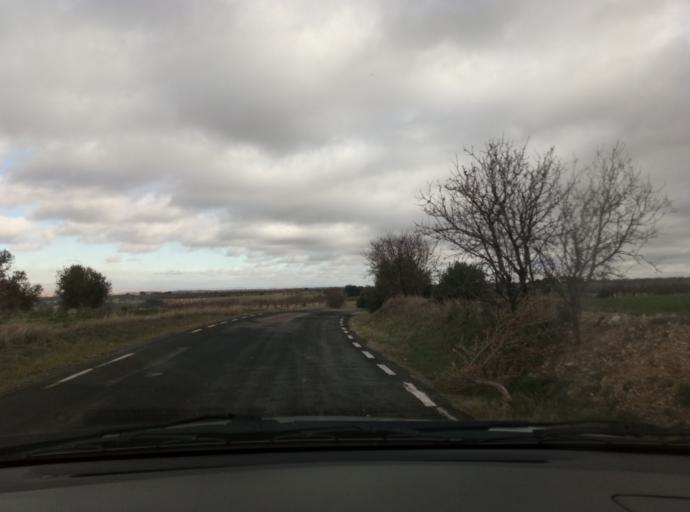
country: ES
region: Catalonia
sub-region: Provincia de Lleida
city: Vallbona de les Monges
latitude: 41.5717
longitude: 1.0719
